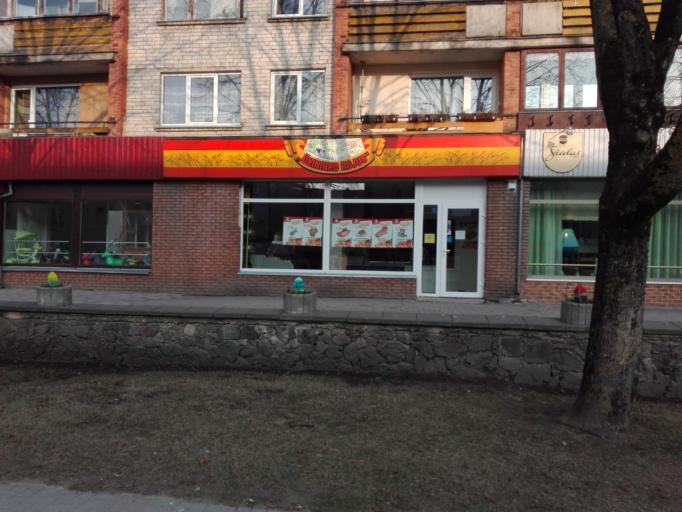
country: LT
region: Panevezys
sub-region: Birzai
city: Birzai
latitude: 56.2001
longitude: 24.7559
